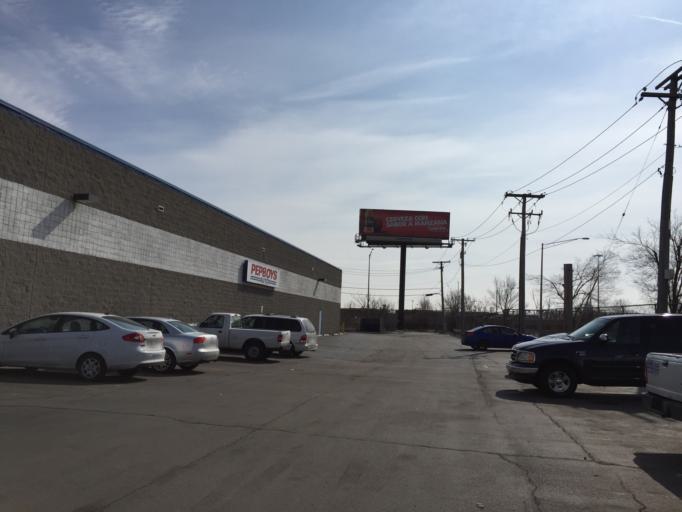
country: US
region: Illinois
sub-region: Cook County
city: Cicero
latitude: 41.8459
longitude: -87.7438
